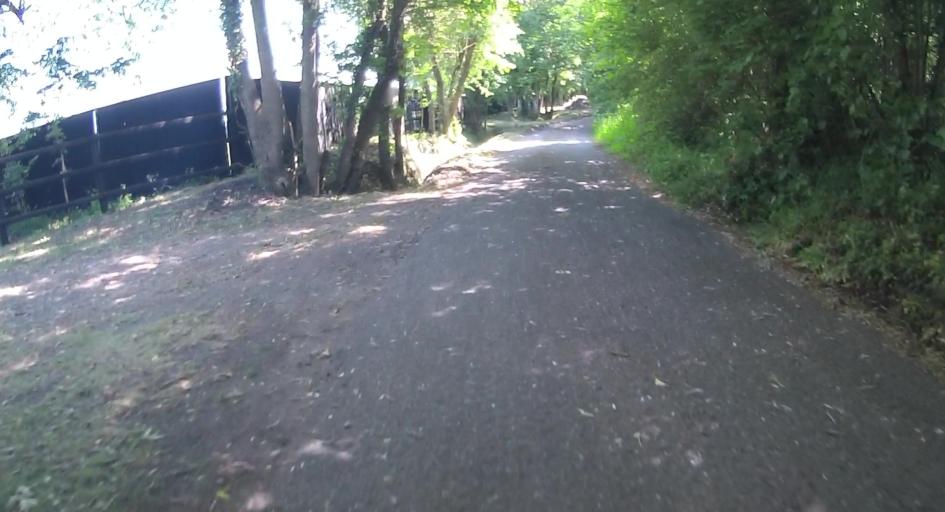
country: GB
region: England
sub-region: Hampshire
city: Kingsclere
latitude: 51.3517
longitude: -1.2722
